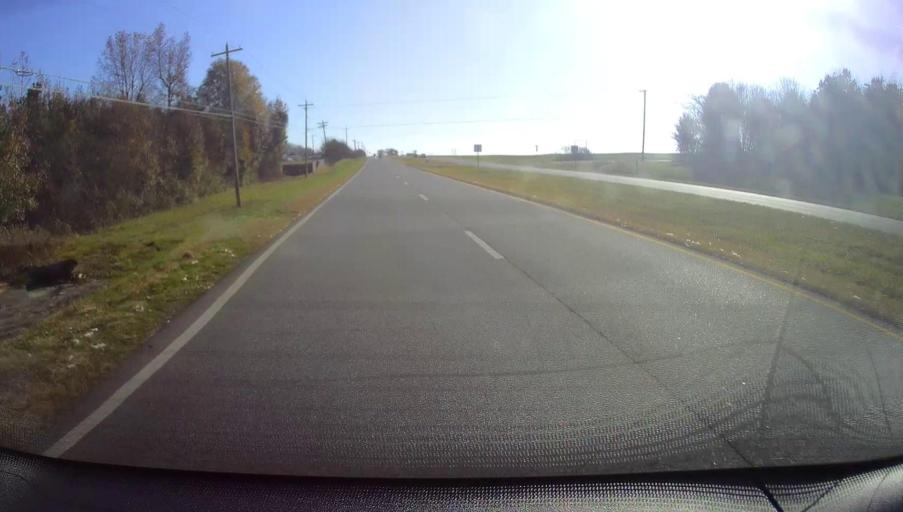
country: US
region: Alabama
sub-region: Limestone County
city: Athens
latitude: 34.7103
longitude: -86.9560
